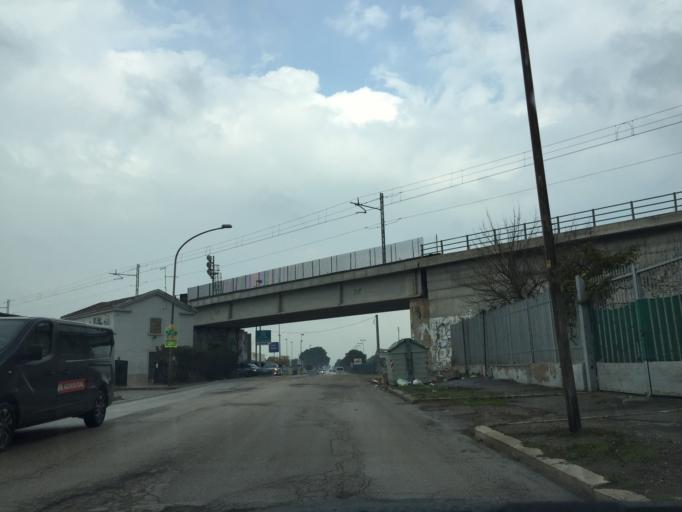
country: IT
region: Apulia
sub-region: Provincia di Foggia
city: Foggia
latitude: 41.4723
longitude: 15.5375
